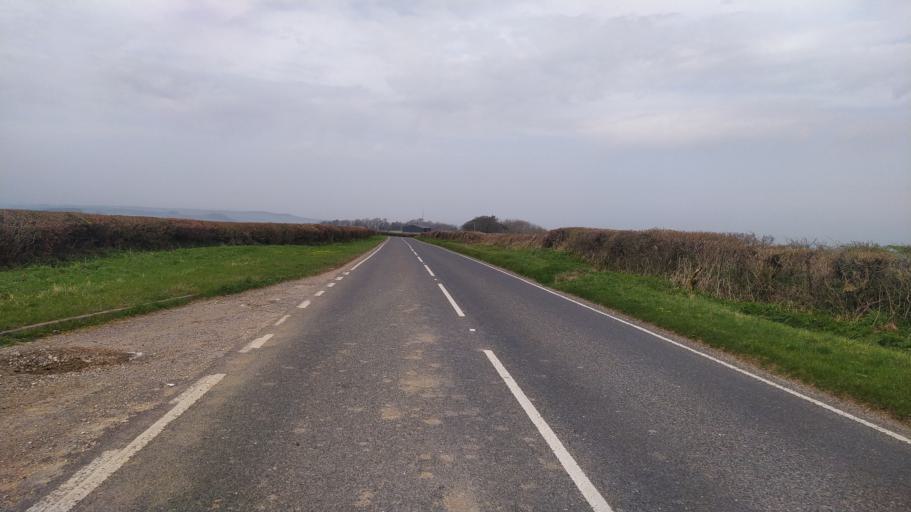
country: GB
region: England
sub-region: Dorset
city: Beaminster
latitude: 50.8426
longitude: -2.7118
